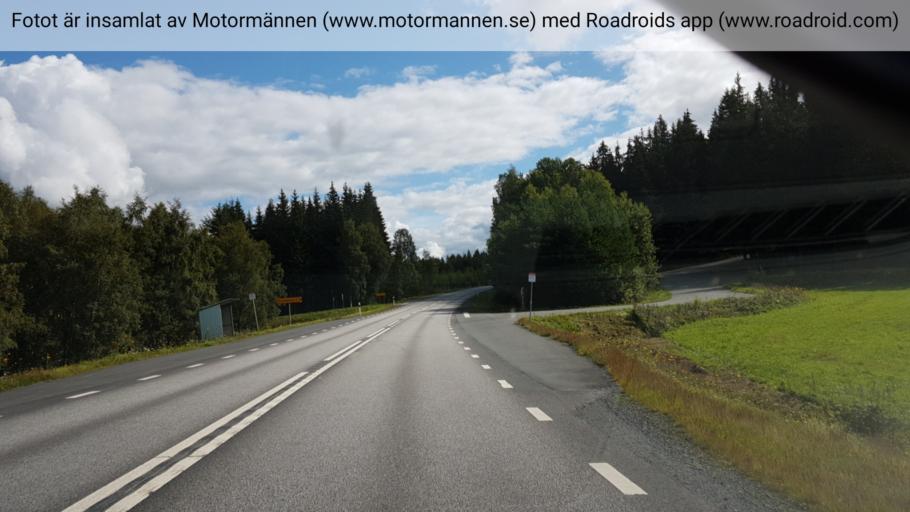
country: SE
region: Joenkoeping
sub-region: Jonkopings Kommun
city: Huskvarna
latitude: 57.7786
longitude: 14.3451
